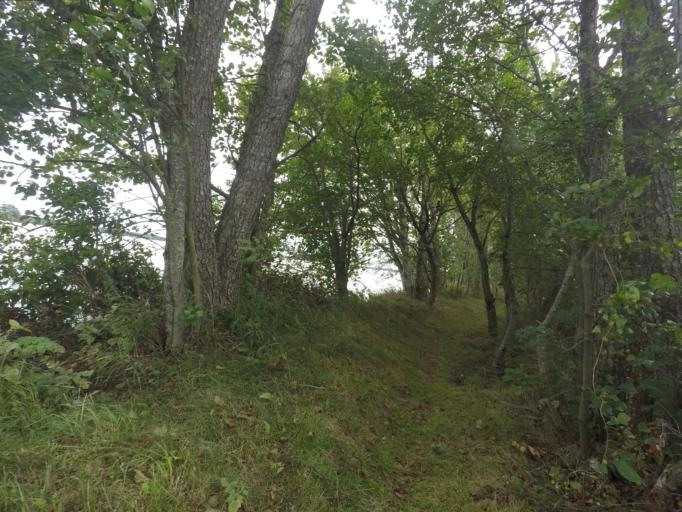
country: SE
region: Vaestmanland
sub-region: Kungsors Kommun
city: Kungsoer
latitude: 59.4707
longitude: 16.0710
